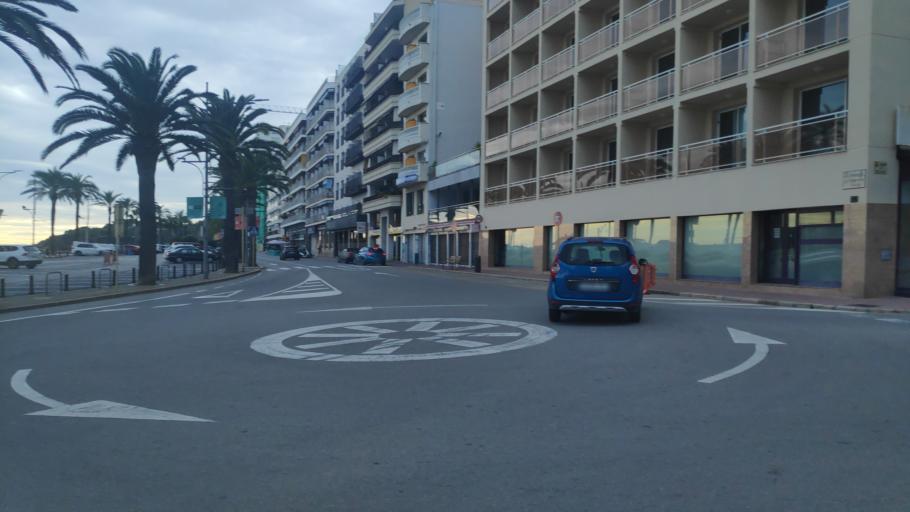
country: ES
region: Catalonia
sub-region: Provincia de Girona
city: Lloret de Mar
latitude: 41.7011
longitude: 2.8556
